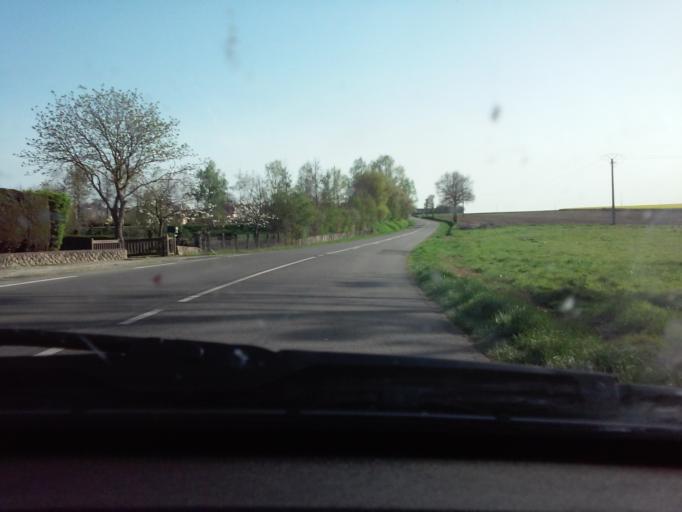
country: FR
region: Brittany
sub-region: Departement d'Ille-et-Vilaine
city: Javene
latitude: 48.3226
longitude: -1.2204
